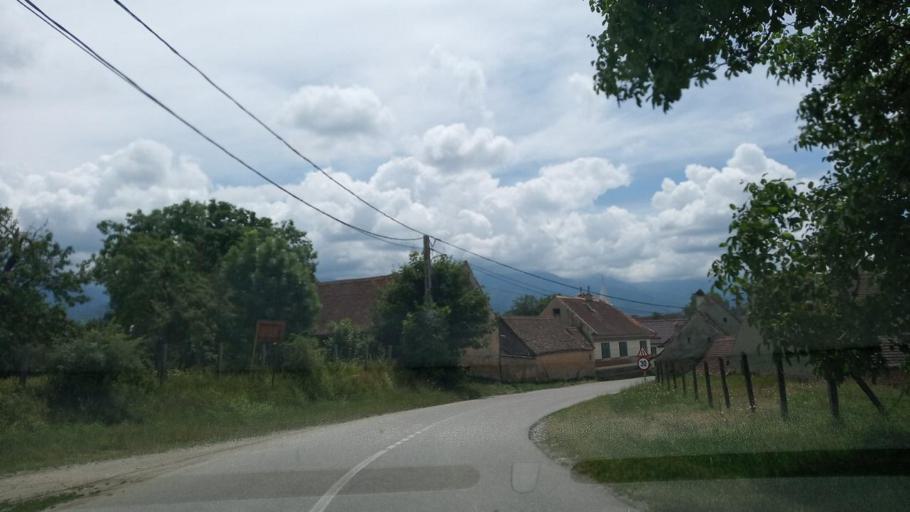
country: RO
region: Sibiu
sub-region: Comuna Porumbacu de Jos
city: Porumbacu de Jos
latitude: 45.7184
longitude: 24.4753
